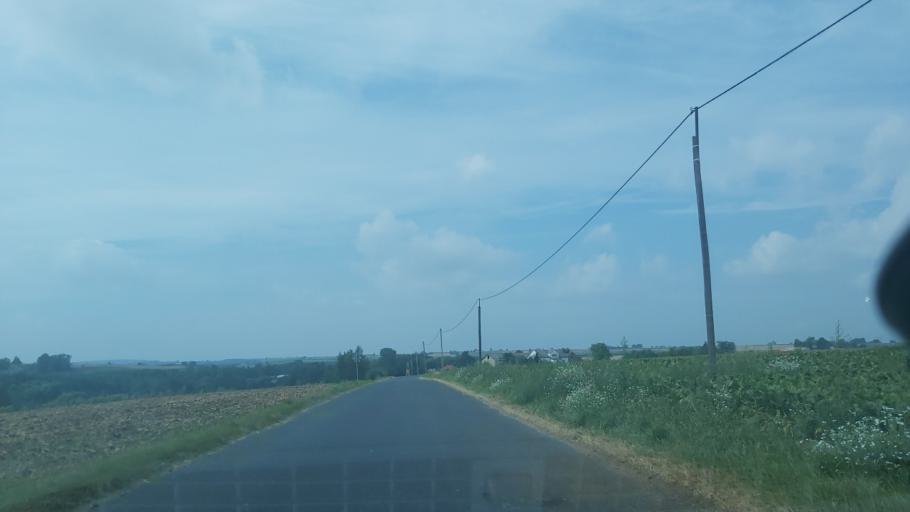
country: PL
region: Kujawsko-Pomorskie
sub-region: Powiat golubsko-dobrzynski
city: Zbojno
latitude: 53.0403
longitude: 19.1689
